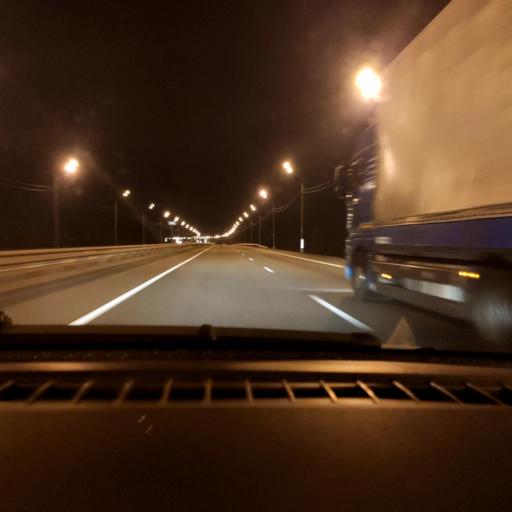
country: RU
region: Lipetsk
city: Khlevnoye
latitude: 52.2722
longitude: 39.0569
